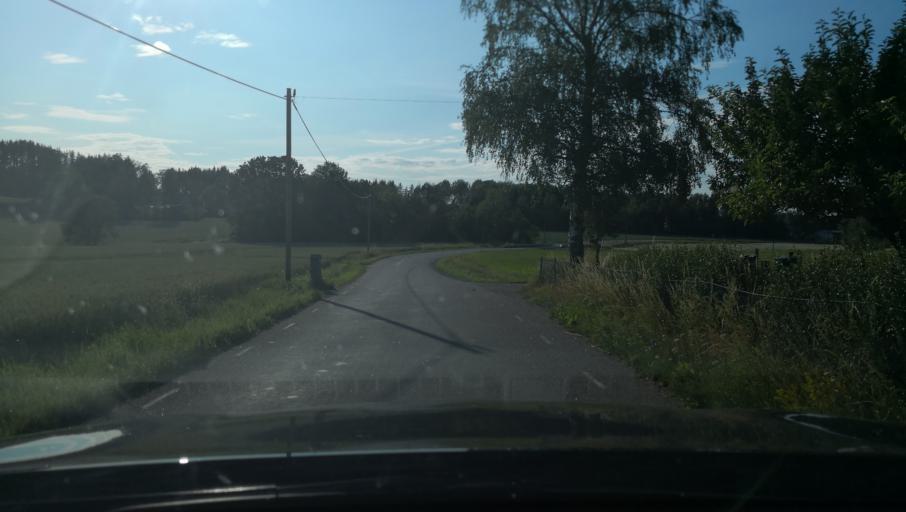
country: SE
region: Uppsala
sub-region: Uppsala Kommun
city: Vattholma
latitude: 59.9317
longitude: 17.8297
